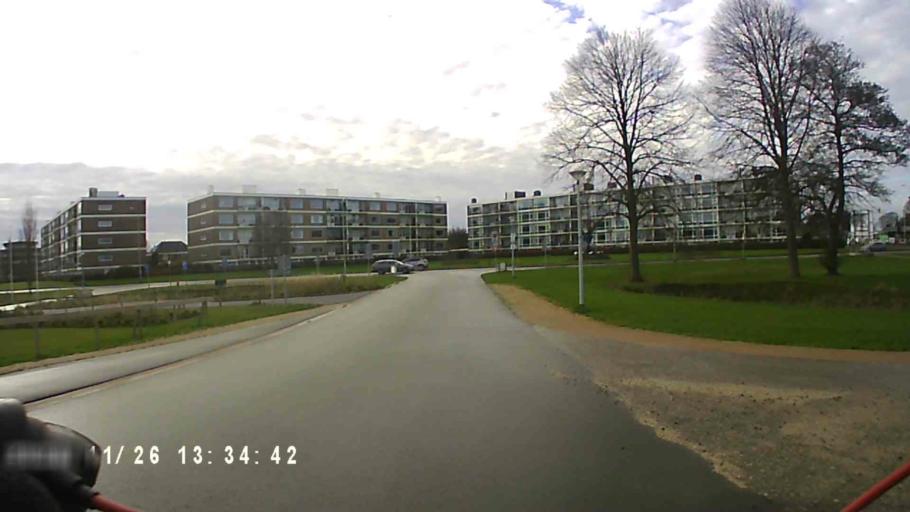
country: NL
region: Groningen
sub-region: Gemeente Delfzijl
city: Delfzijl
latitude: 53.3361
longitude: 6.9262
